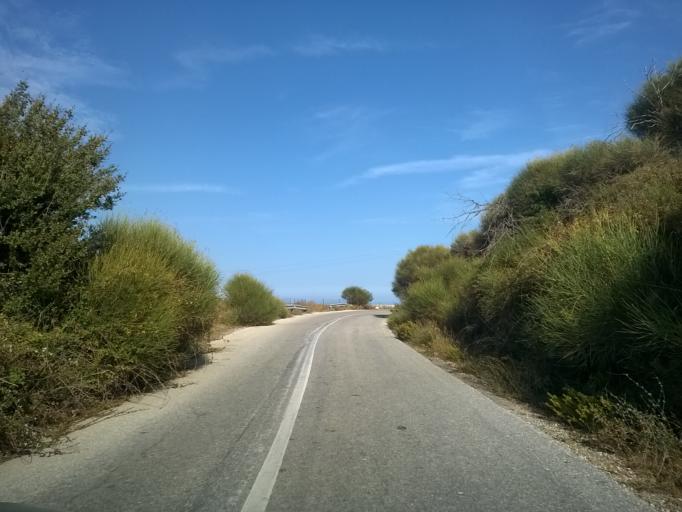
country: GR
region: South Aegean
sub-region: Nomos Kykladon
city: Filotion
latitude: 37.1356
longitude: 25.5369
